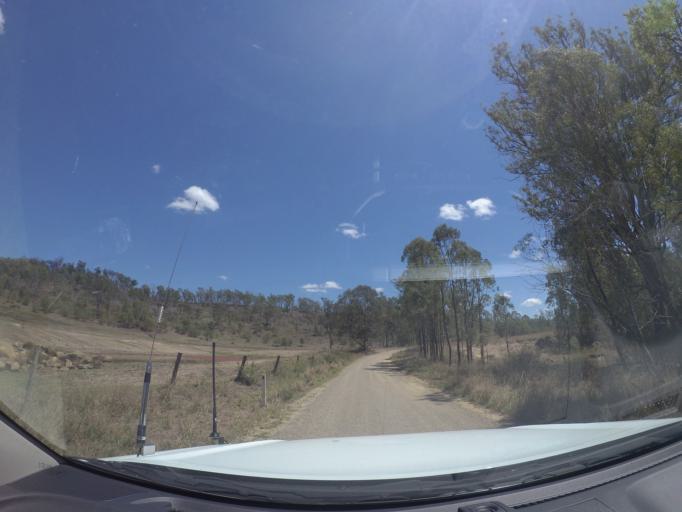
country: AU
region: Queensland
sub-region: Logan
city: North Maclean
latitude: -27.8222
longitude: 152.8585
